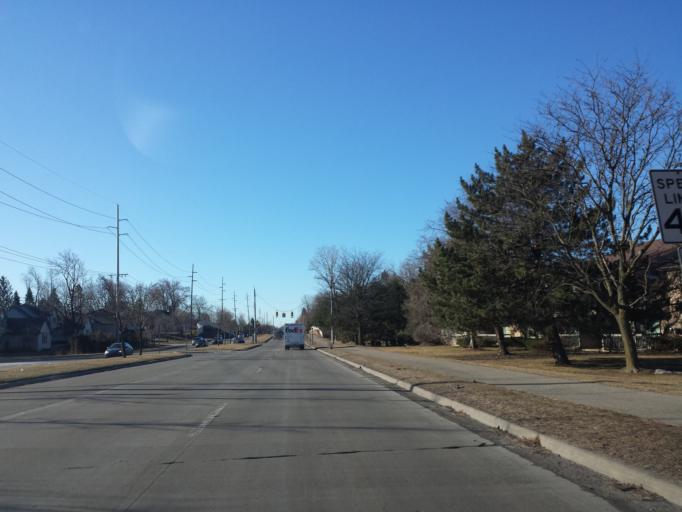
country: US
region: Michigan
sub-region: Oakland County
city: Rochester Hills
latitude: 42.6747
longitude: -83.1535
